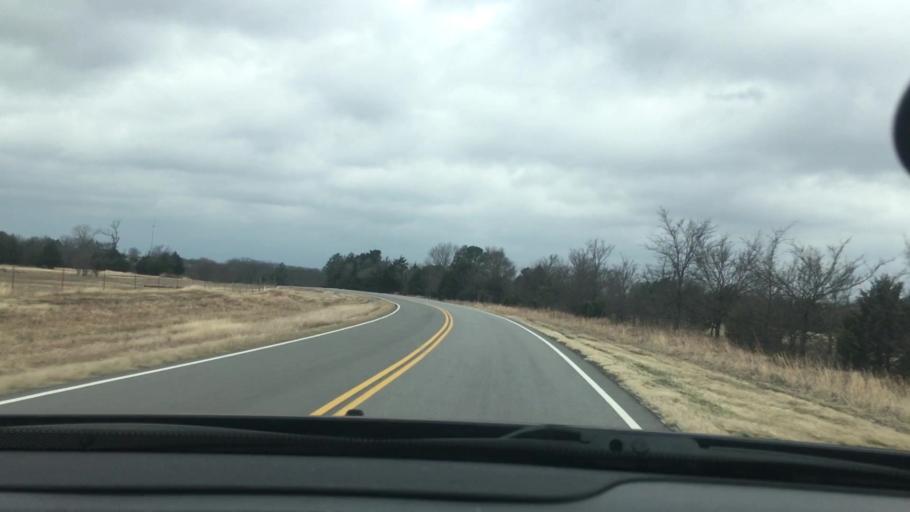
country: US
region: Oklahoma
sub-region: Atoka County
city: Atoka
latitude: 34.3780
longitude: -96.2638
